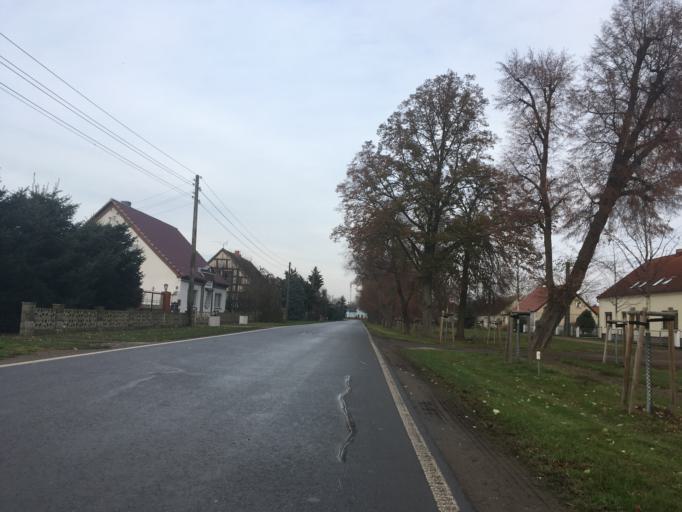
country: DE
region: Brandenburg
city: Neulewin
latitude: 52.7128
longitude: 14.3018
